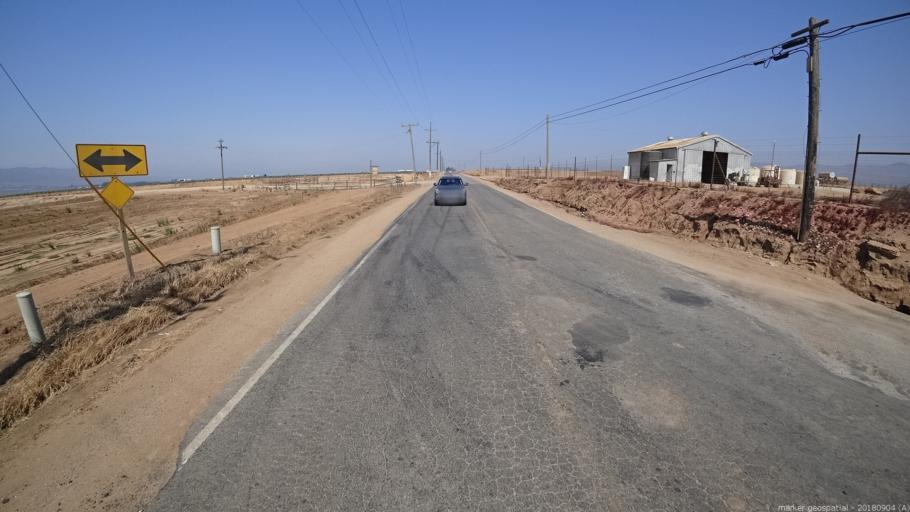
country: US
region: California
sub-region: Monterey County
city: Chualar
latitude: 36.5571
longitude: -121.4784
